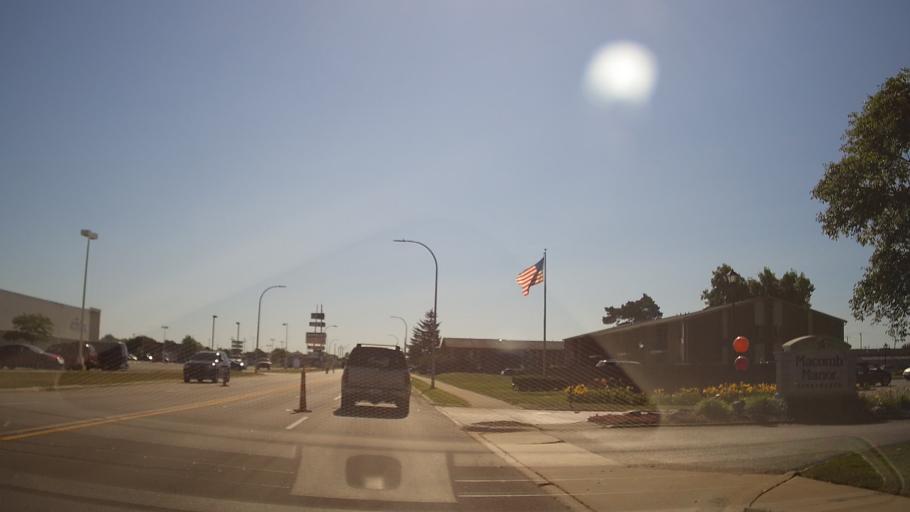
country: US
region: Michigan
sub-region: Macomb County
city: Fraser
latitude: 42.5322
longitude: -82.9182
